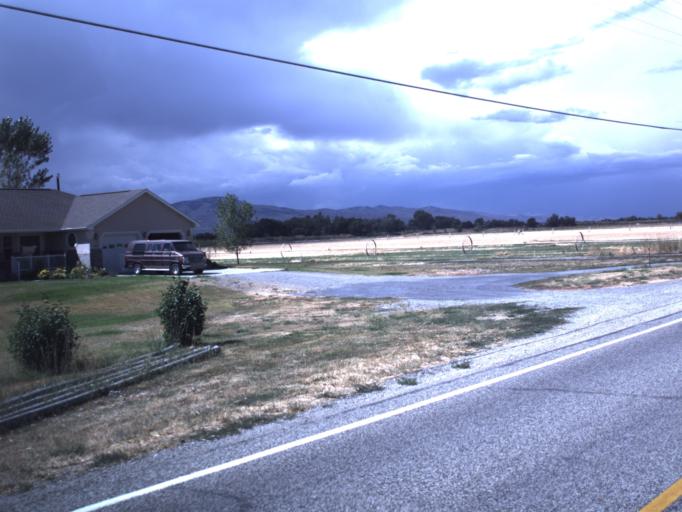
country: US
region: Utah
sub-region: Box Elder County
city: Honeyville
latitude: 41.6799
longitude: -112.0898
